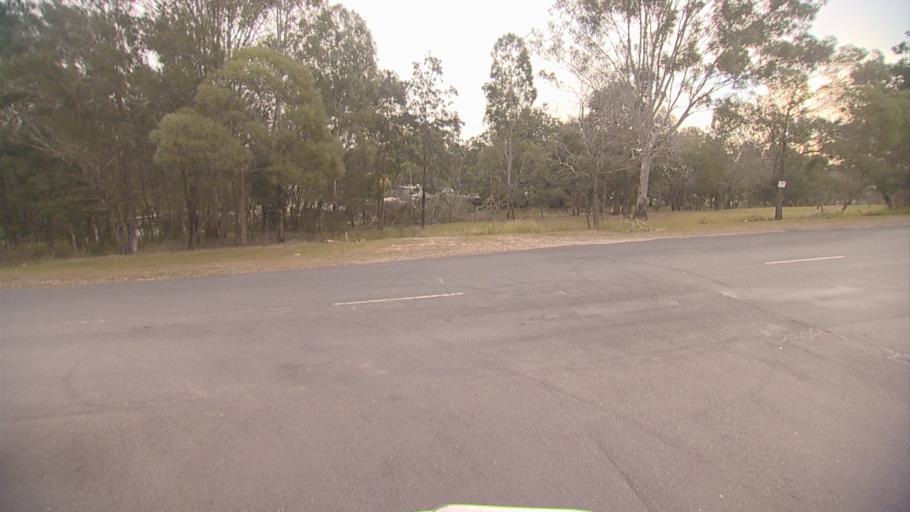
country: AU
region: Queensland
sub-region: Logan
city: Waterford West
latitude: -27.7085
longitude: 153.1483
